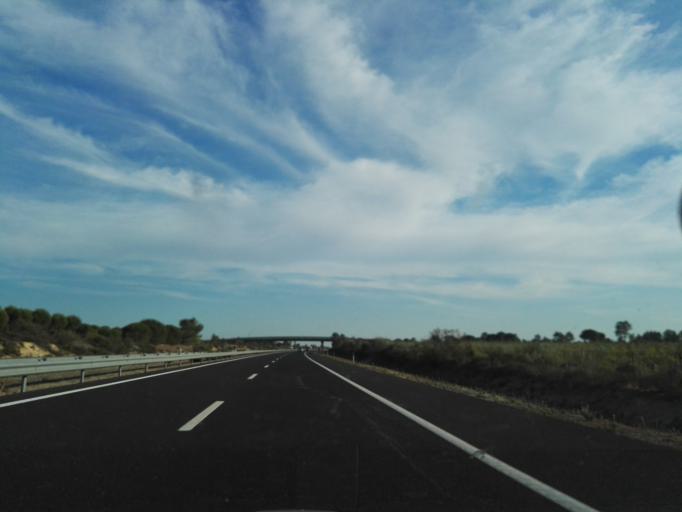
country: PT
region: Santarem
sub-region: Benavente
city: Poceirao
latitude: 38.7903
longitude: -8.6897
